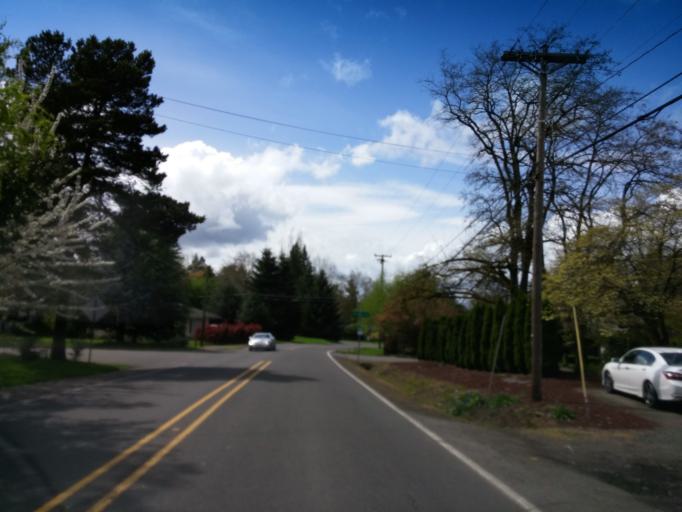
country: US
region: Oregon
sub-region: Washington County
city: Cedar Hills
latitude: 45.5001
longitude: -122.7998
